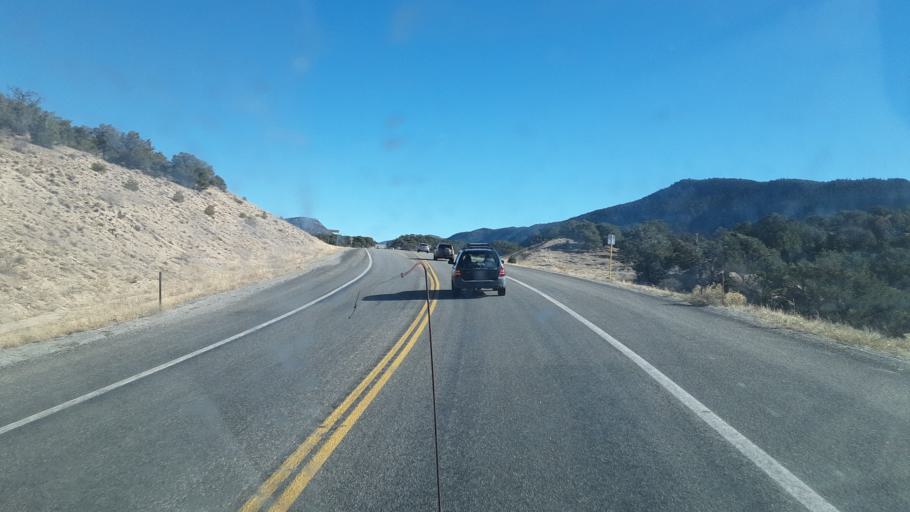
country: US
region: Colorado
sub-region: Chaffee County
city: Buena Vista
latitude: 38.8143
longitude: -106.0877
